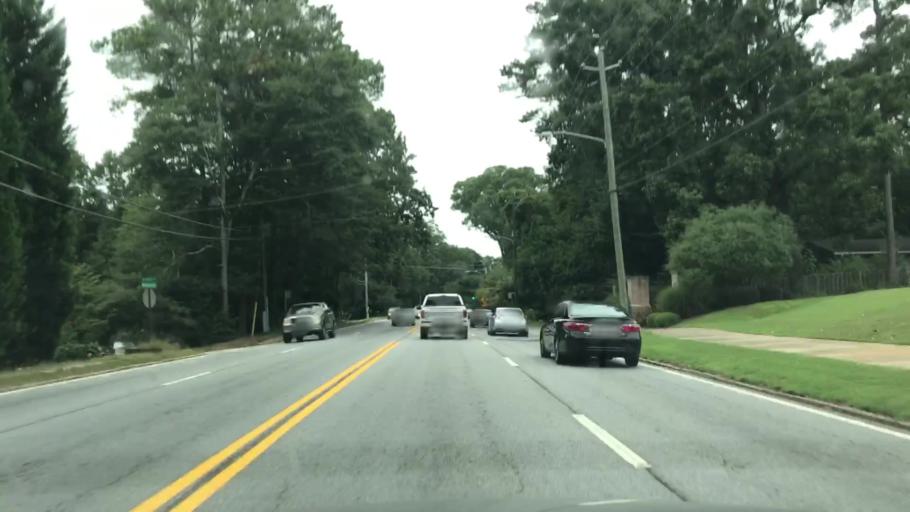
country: US
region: Georgia
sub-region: DeKalb County
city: North Druid Hills
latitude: 33.8113
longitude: -84.2868
